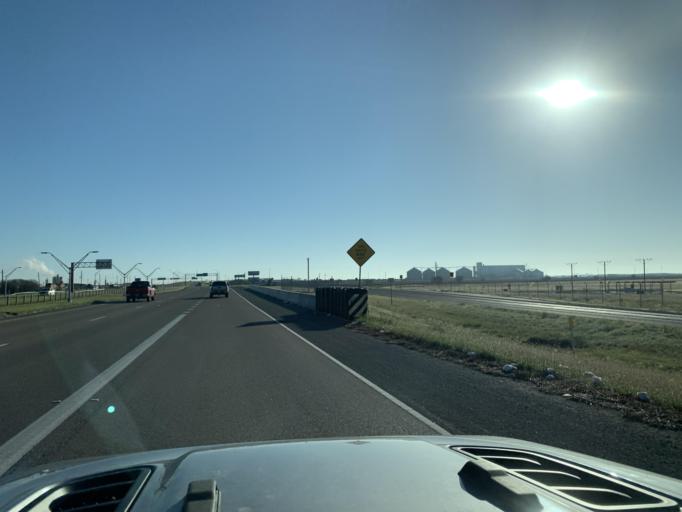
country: US
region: Texas
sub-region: Nueces County
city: Corpus Christi
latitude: 27.7848
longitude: -97.4973
